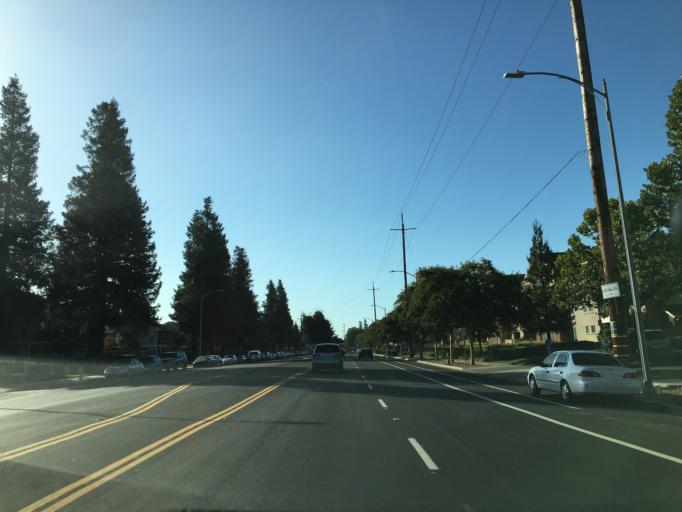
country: US
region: California
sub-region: Santa Clara County
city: San Jose
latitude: 37.3698
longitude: -121.8715
